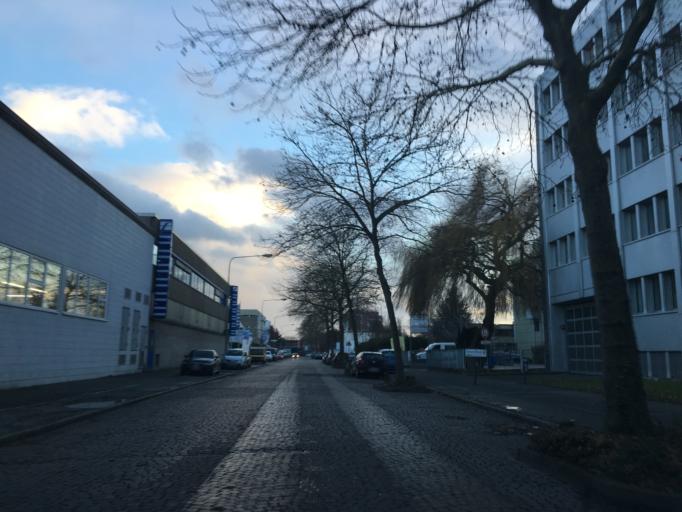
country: DE
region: Hesse
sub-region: Regierungsbezirk Darmstadt
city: Offenbach
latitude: 50.1317
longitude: 8.7462
